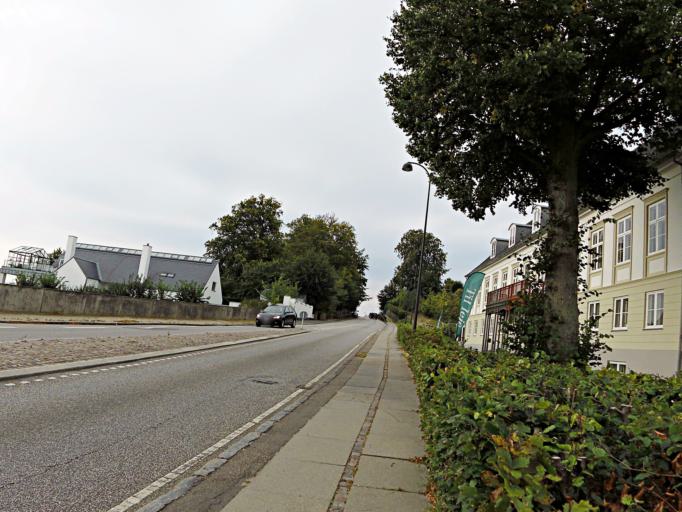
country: DK
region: Capital Region
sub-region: Rudersdal Kommune
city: Trorod
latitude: 55.8183
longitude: 12.5748
